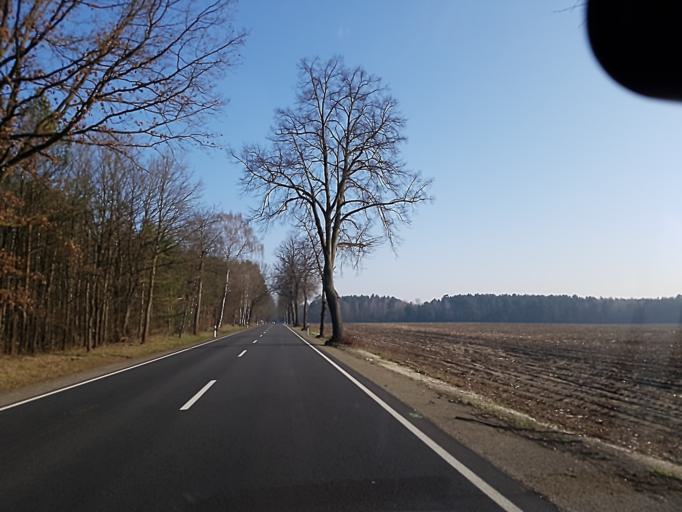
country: DE
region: Brandenburg
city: Bronkow
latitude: 51.6848
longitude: 13.9156
